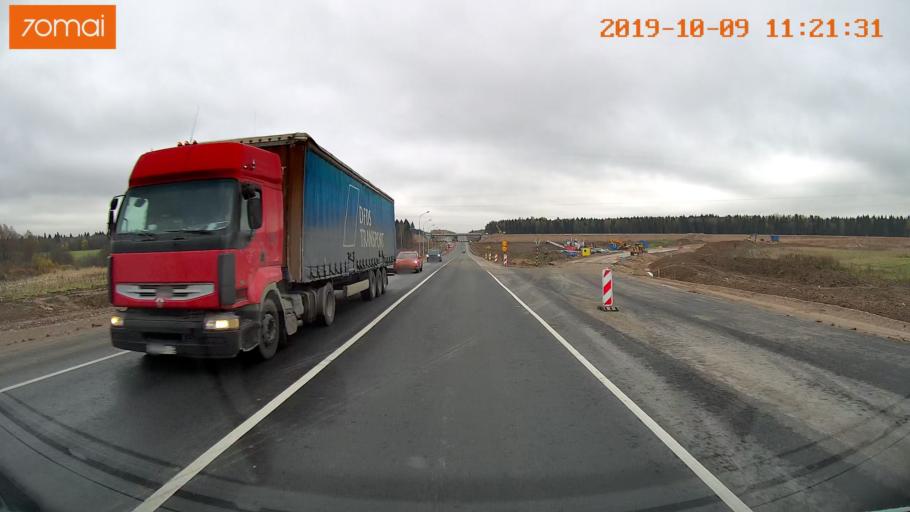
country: RU
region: Vologda
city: Vologda
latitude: 59.1389
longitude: 39.9501
